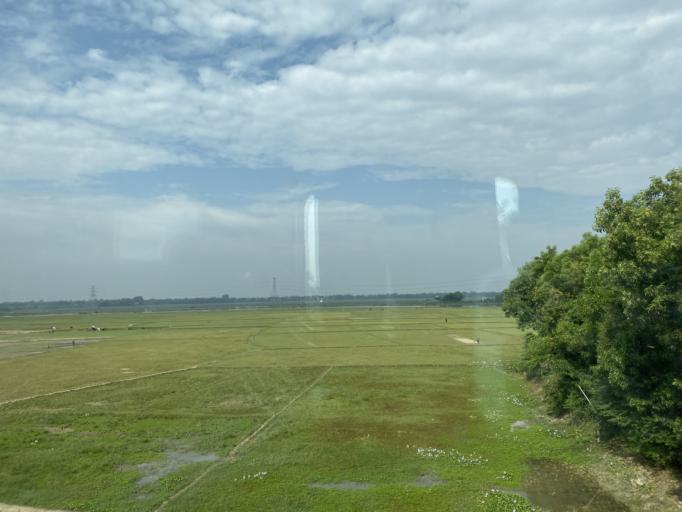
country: IN
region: Tripura
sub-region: West Tripura
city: Agartala
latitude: 23.8828
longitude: 91.2057
